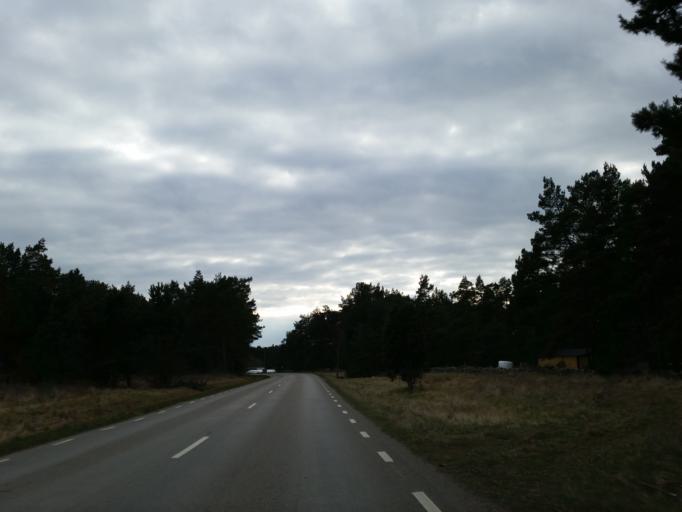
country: SE
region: Kalmar
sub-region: Morbylanga Kommun
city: Sodra Sandby
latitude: 56.5877
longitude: 16.6277
